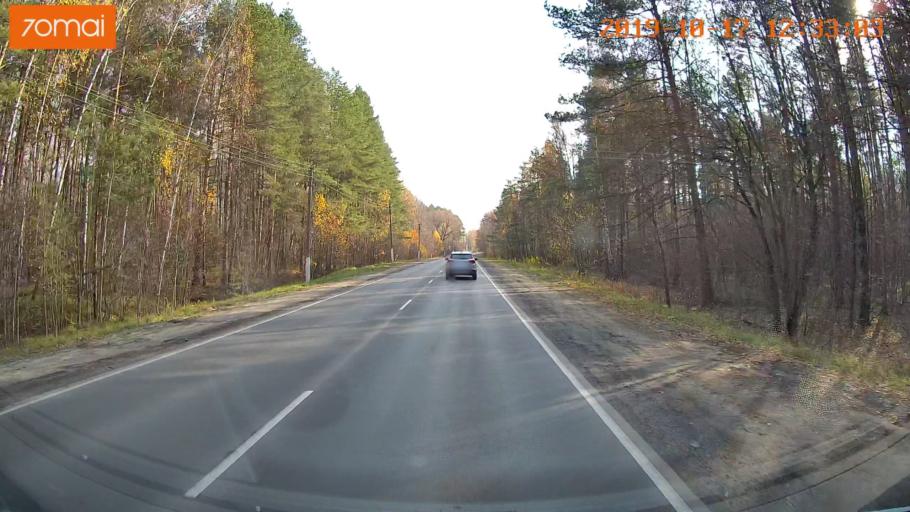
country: RU
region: Rjazan
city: Kasimov
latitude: 54.9577
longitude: 41.3497
